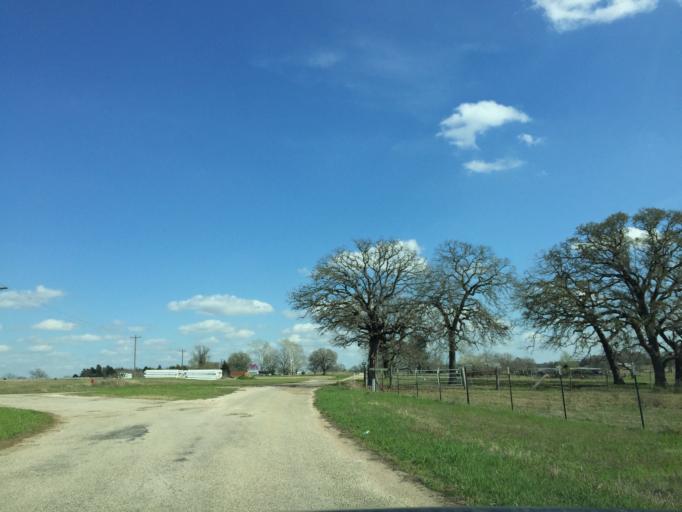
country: US
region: Texas
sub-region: Milam County
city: Thorndale
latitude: 30.5937
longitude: -97.1335
